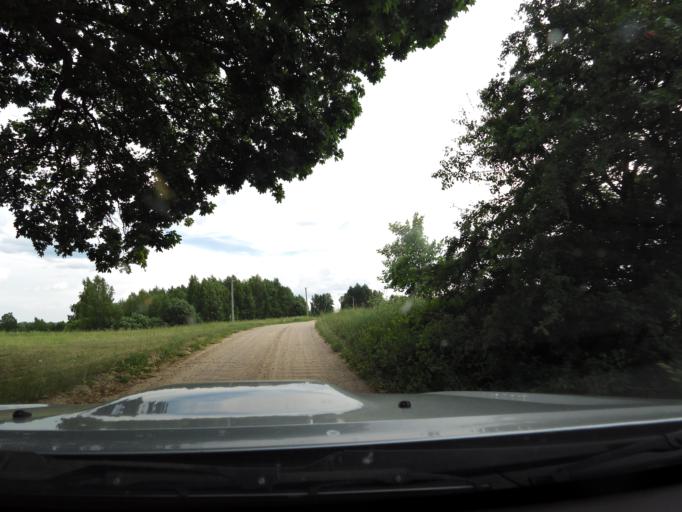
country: LT
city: Grigiskes
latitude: 54.7911
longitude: 25.0141
